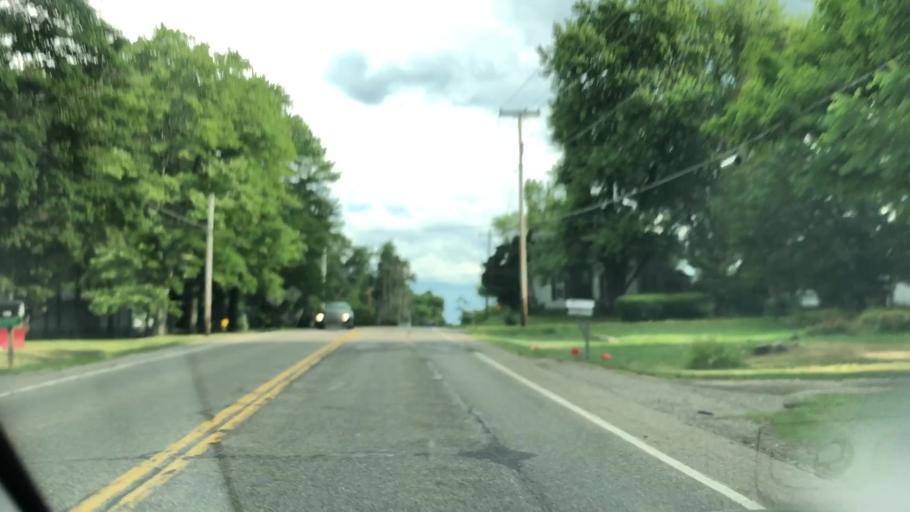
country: US
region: Ohio
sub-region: Summit County
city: Greensburg
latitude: 40.9219
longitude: -81.4632
